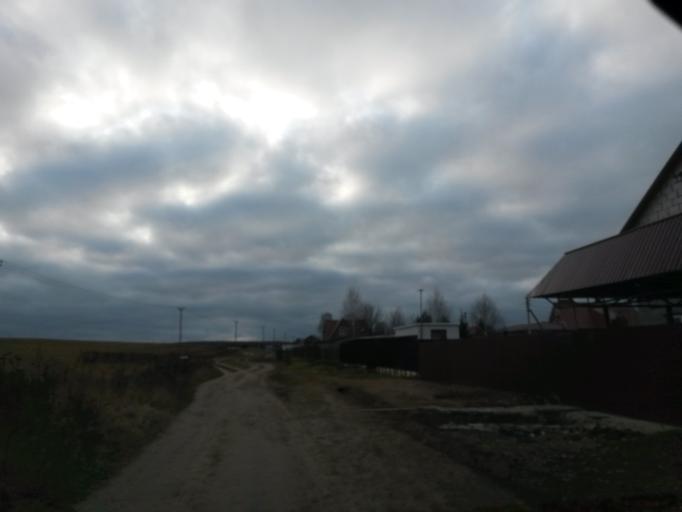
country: RU
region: Moskovskaya
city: Lyubuchany
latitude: 55.2571
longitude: 37.5981
